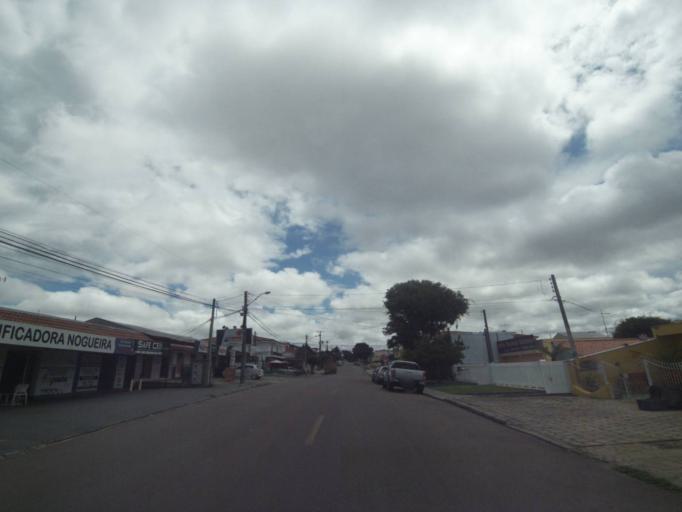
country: BR
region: Parana
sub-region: Curitiba
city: Curitiba
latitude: -25.4803
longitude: -49.2800
